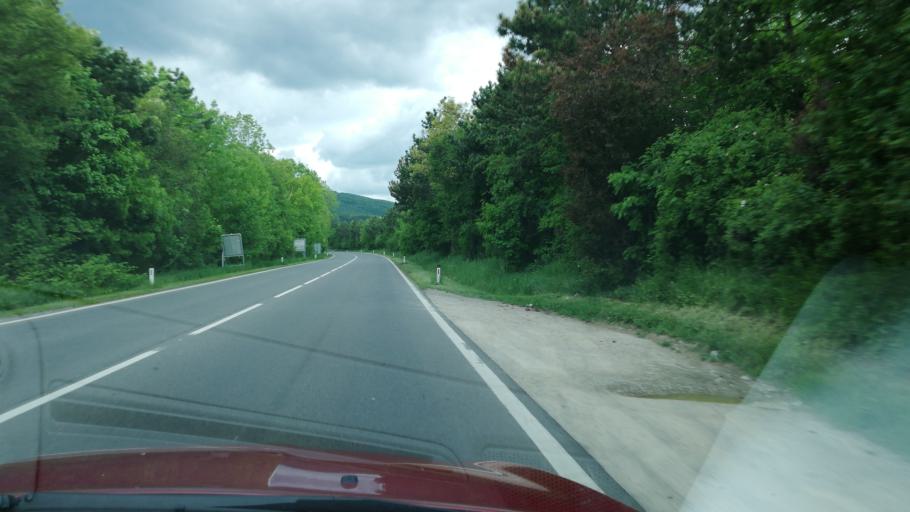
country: AT
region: Lower Austria
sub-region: Politischer Bezirk Baden
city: Baden
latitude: 47.9967
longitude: 16.2258
